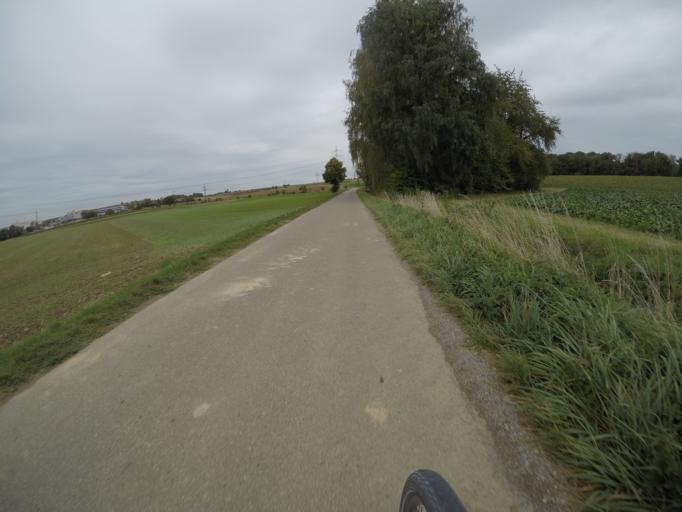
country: DE
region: Baden-Wuerttemberg
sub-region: Regierungsbezirk Stuttgart
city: Leonberg
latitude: 48.8367
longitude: 8.9932
